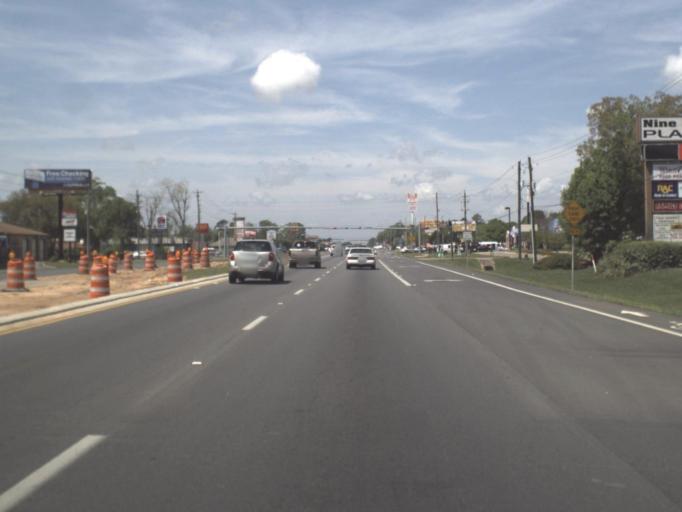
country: US
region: Florida
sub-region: Escambia County
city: Ensley
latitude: 30.5330
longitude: -87.2598
